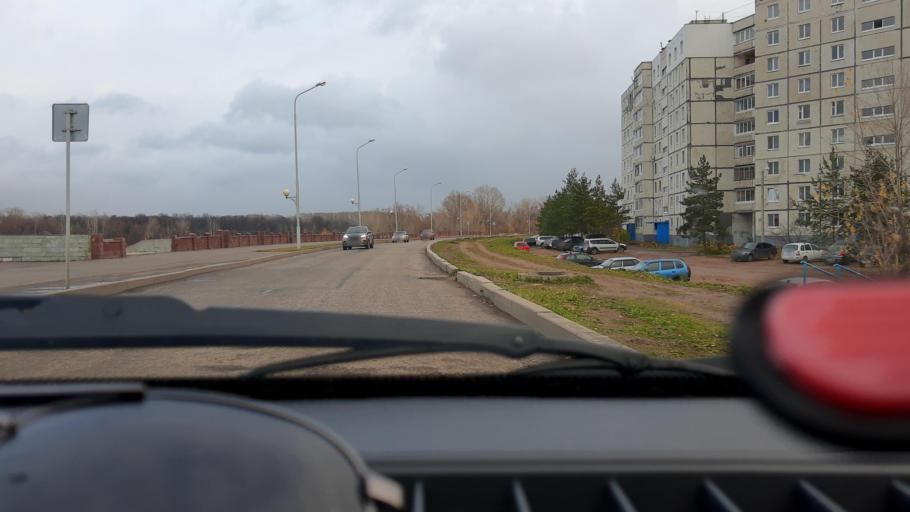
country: RU
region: Bashkortostan
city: Ufa
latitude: 54.7764
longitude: 56.0830
